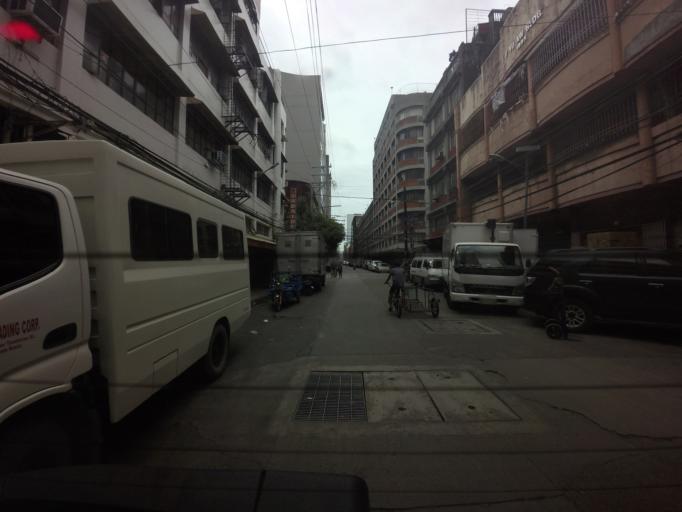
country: PH
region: Metro Manila
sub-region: City of Manila
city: Manila
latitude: 14.6005
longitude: 120.9695
